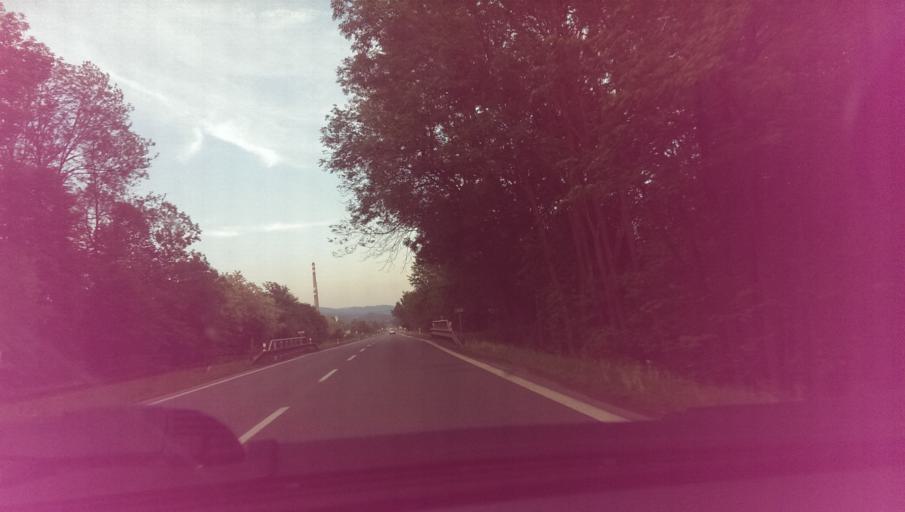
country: CZ
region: Zlin
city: Zubri
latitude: 49.4600
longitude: 18.1089
